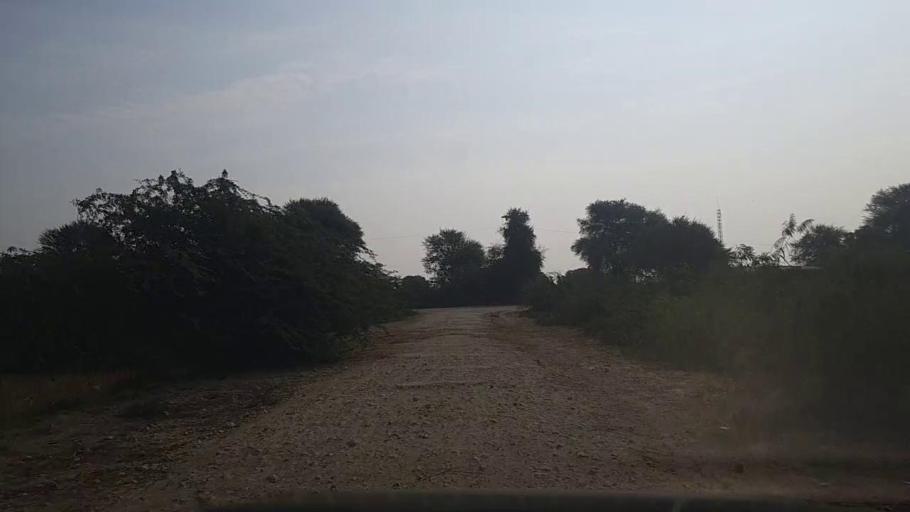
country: PK
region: Sindh
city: Bulri
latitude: 24.9696
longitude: 68.3306
